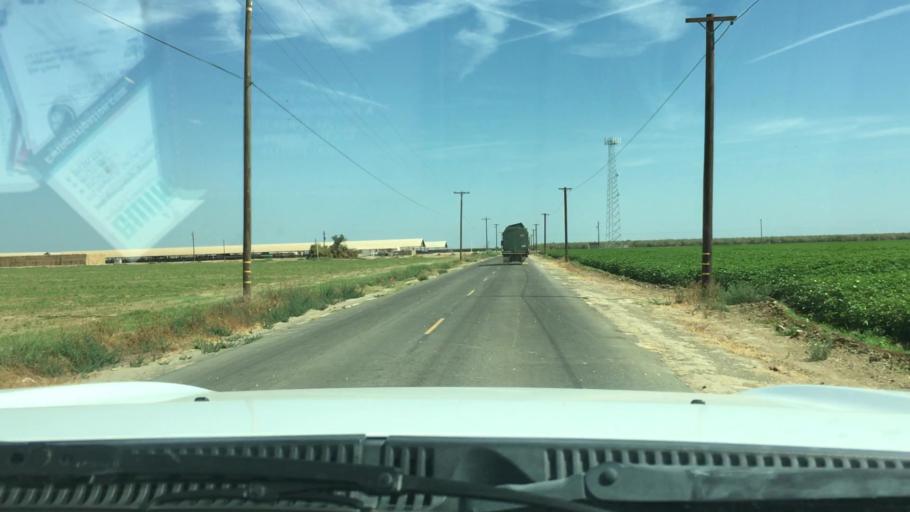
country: US
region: California
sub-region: Kern County
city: Shafter
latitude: 35.4680
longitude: -119.3681
